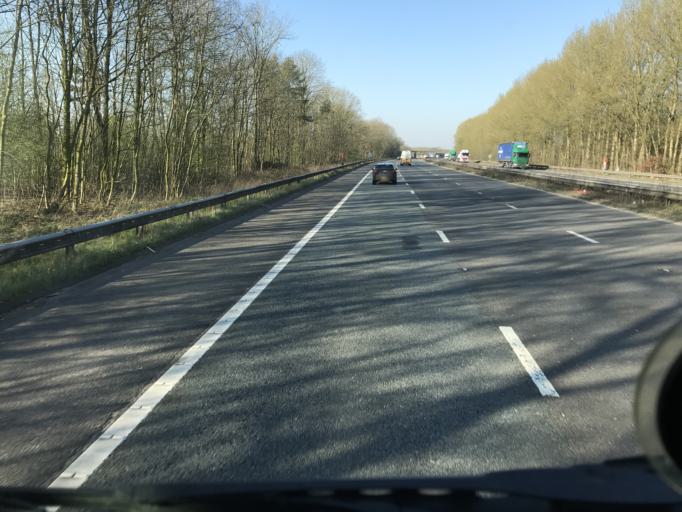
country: GB
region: England
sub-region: Borough of Halton
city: Daresbury
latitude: 53.3306
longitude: -2.6144
